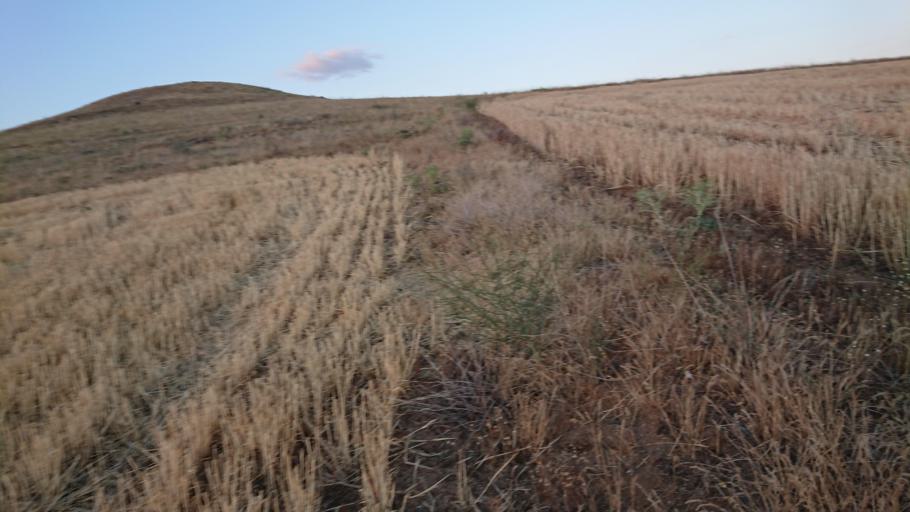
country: TR
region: Aksaray
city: Agacoren
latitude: 38.9119
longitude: 33.8910
